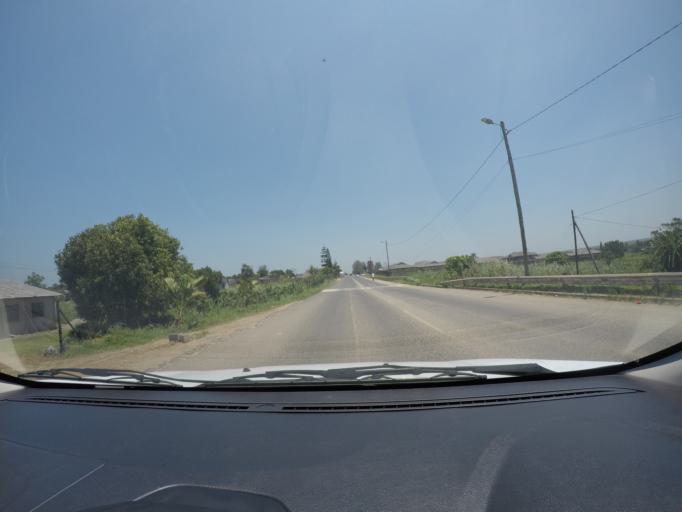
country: ZA
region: KwaZulu-Natal
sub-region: uThungulu District Municipality
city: eSikhawini
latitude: -28.8873
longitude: 31.8975
